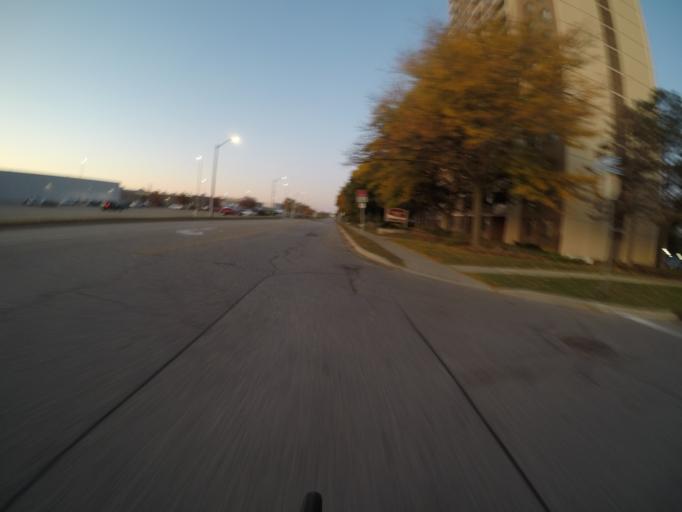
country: CA
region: Ontario
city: Kitchener
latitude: 43.4267
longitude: -80.4387
